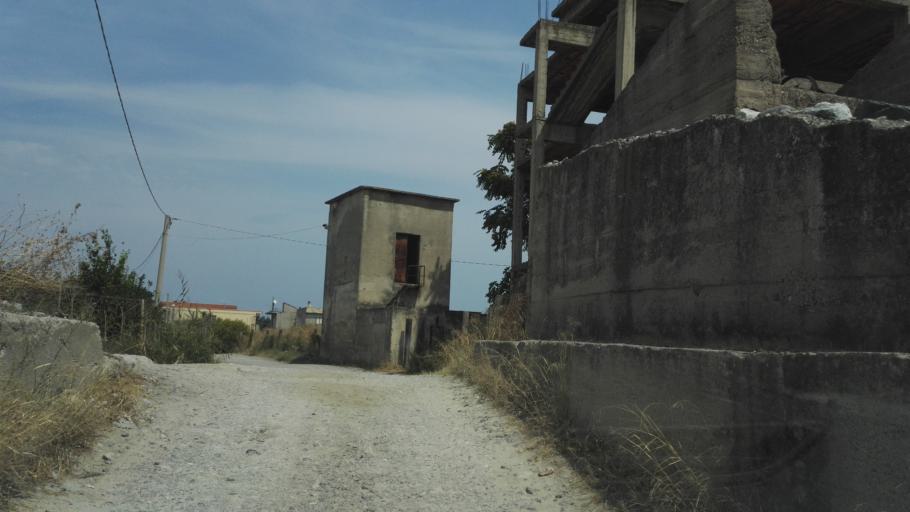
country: IT
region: Calabria
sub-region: Provincia di Reggio Calabria
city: Monasterace Marina
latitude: 38.4280
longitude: 16.5676
